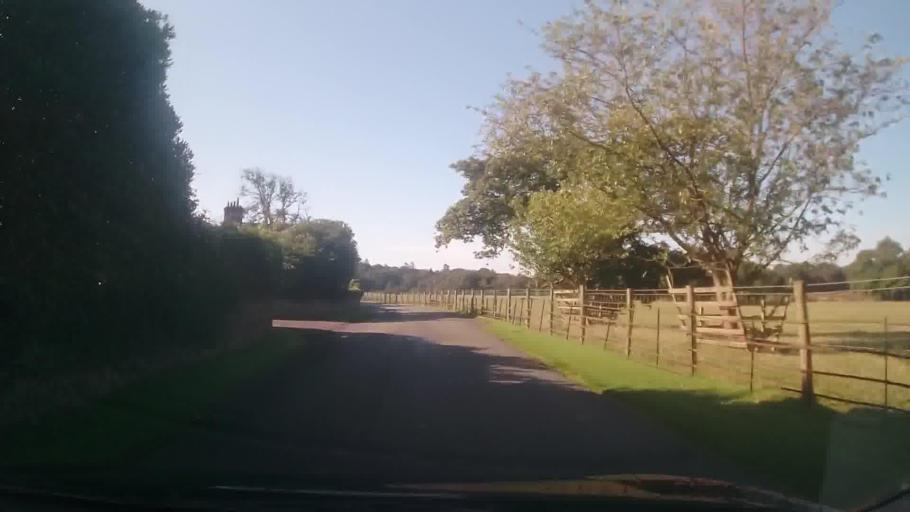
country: GB
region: England
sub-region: Cumbria
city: Seascale
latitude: 54.3981
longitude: -3.3782
